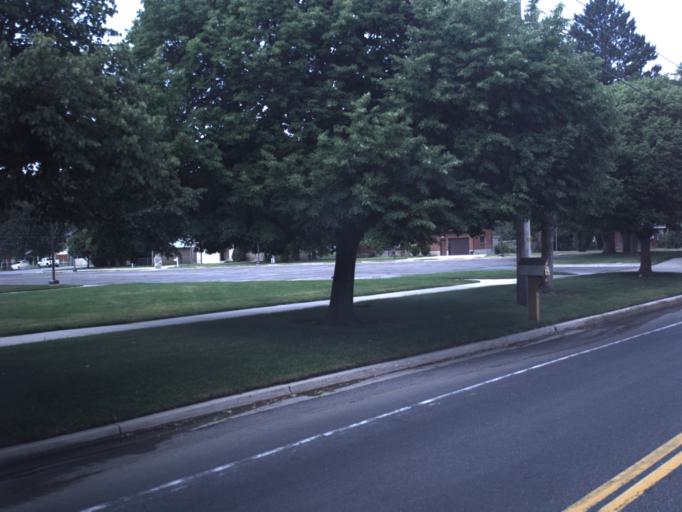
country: US
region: Utah
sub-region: Davis County
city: South Weber
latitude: 41.1341
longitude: -111.9434
